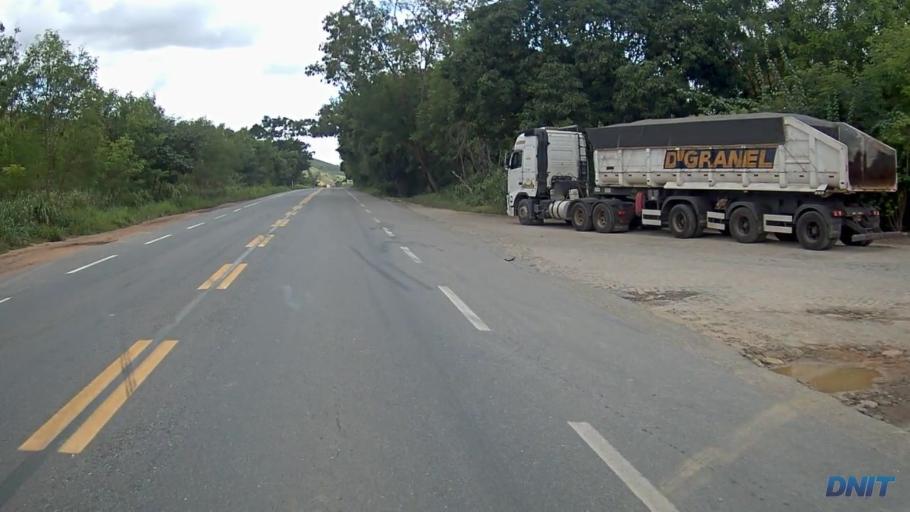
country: BR
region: Minas Gerais
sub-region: Governador Valadares
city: Governador Valadares
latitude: -18.9377
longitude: -42.0542
